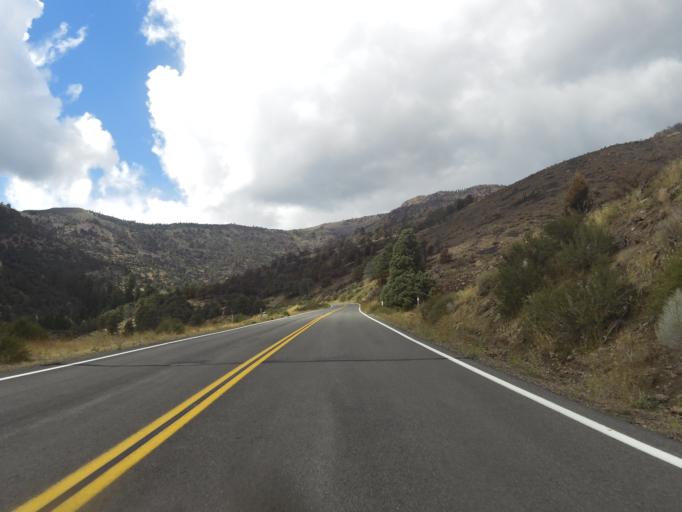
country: US
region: Nevada
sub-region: Lyon County
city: Smith Valley
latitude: 38.6554
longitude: -119.5865
